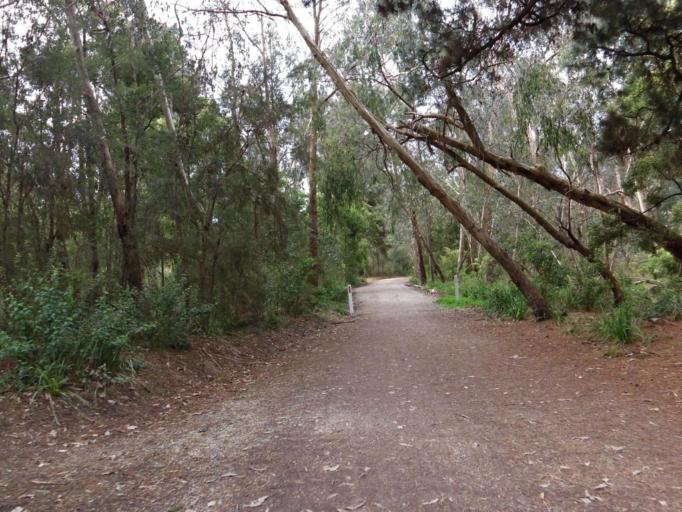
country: AU
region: Victoria
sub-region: Maroondah
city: Ringwood East
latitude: -37.7982
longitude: 145.2489
